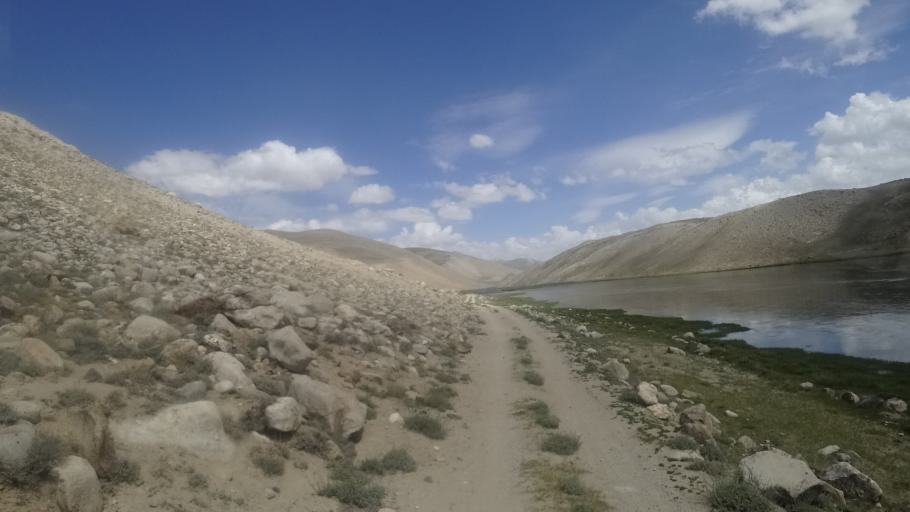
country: TJ
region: Gorno-Badakhshan
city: Murghob
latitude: 37.4733
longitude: 73.4466
